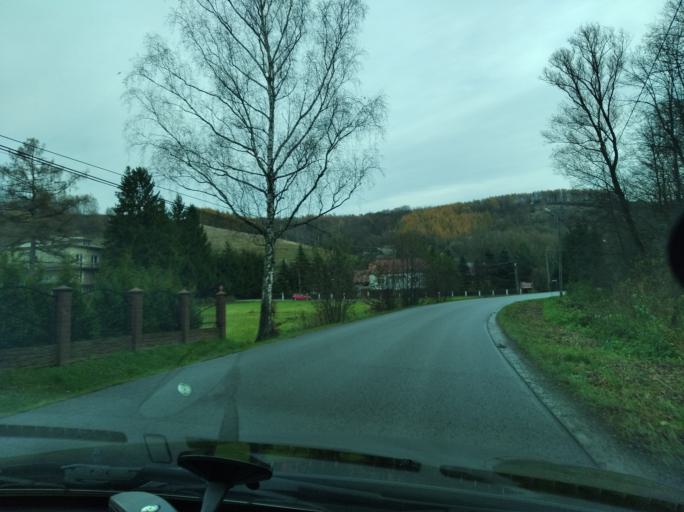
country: PL
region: Subcarpathian Voivodeship
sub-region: Powiat ropczycko-sedziszowski
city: Iwierzyce
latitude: 49.9478
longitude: 21.7476
